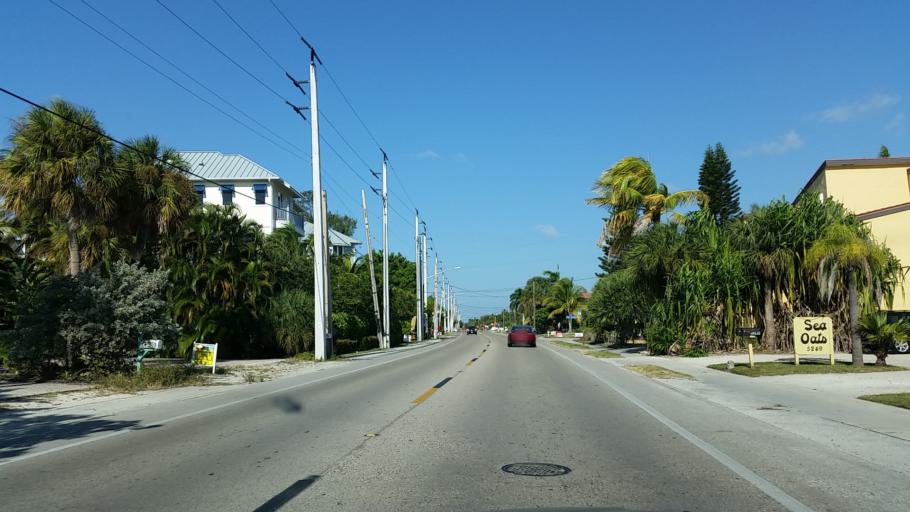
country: US
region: Florida
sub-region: Lee County
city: Fort Myers Beach
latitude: 26.4326
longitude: -81.9158
